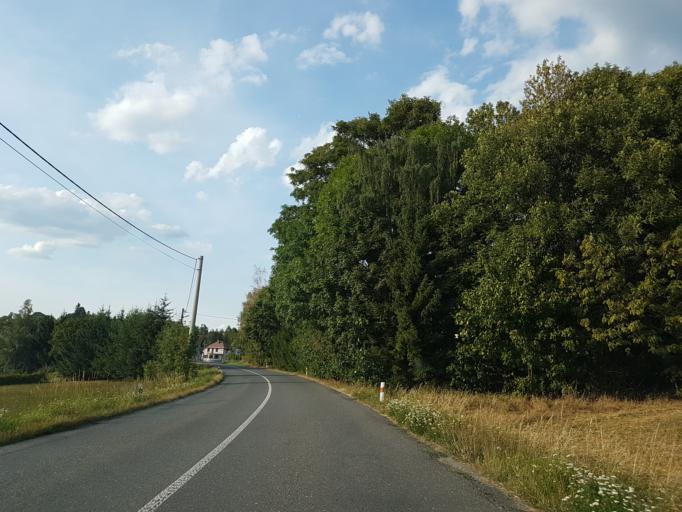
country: CZ
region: Liberecky
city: Mala Skala
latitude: 50.6797
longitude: 15.1846
